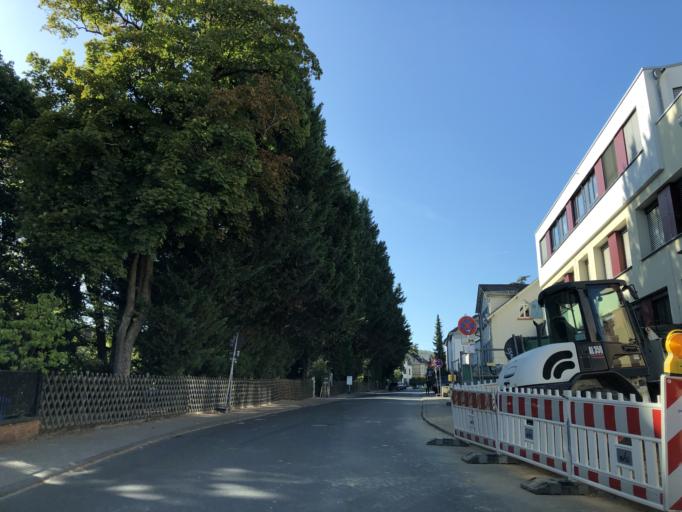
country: DE
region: Hesse
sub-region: Regierungsbezirk Darmstadt
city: Hofheim am Taunus
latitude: 50.0884
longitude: 8.4412
